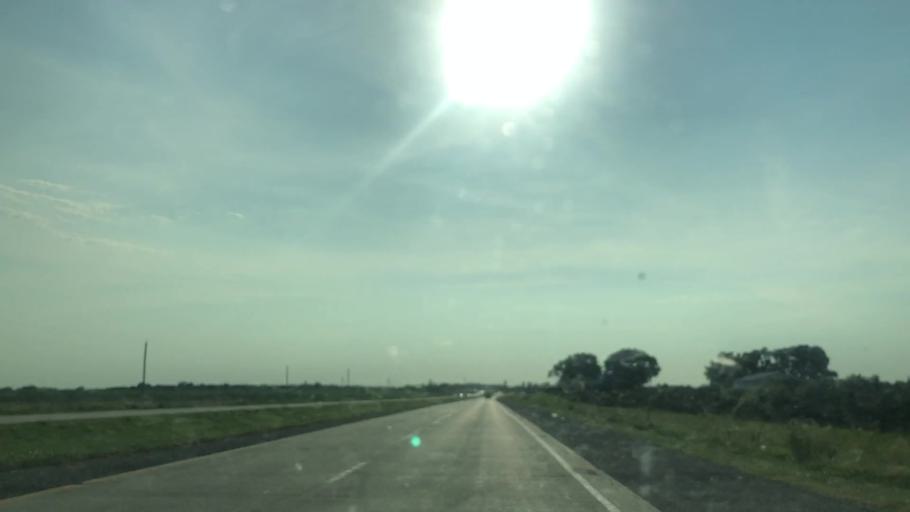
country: US
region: Iowa
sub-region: Story County
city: Nevada
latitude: 42.0080
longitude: -93.4164
